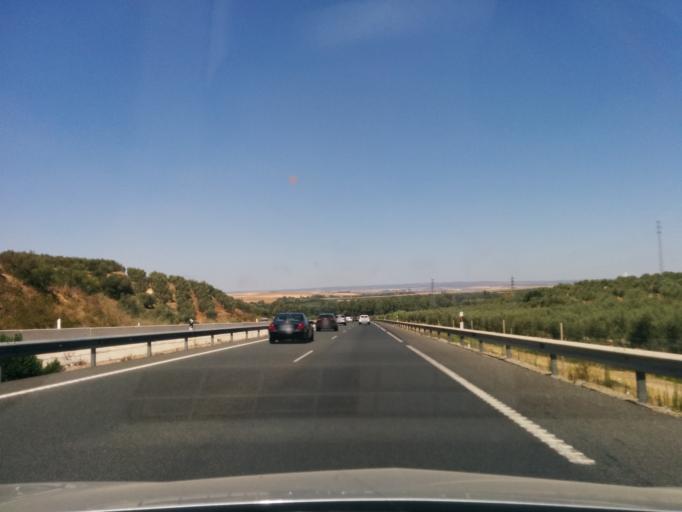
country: ES
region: Andalusia
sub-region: Provincia de Sevilla
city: Sanlucar la Mayor
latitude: 37.3674
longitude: -6.2163
